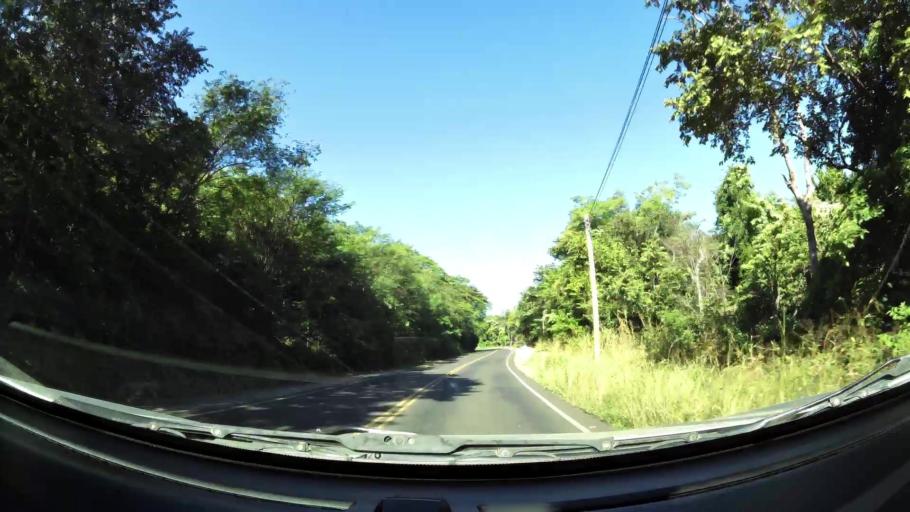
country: CR
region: Guanacaste
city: Belen
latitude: 10.3699
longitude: -85.6353
